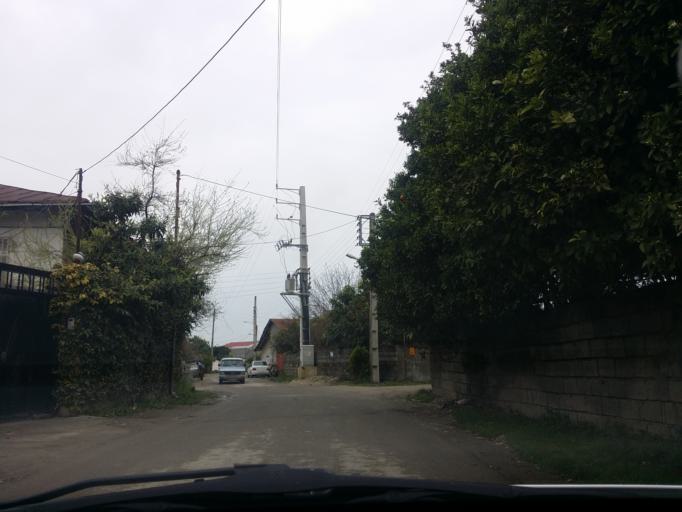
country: IR
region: Mazandaran
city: Chalus
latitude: 36.6671
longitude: 51.3803
